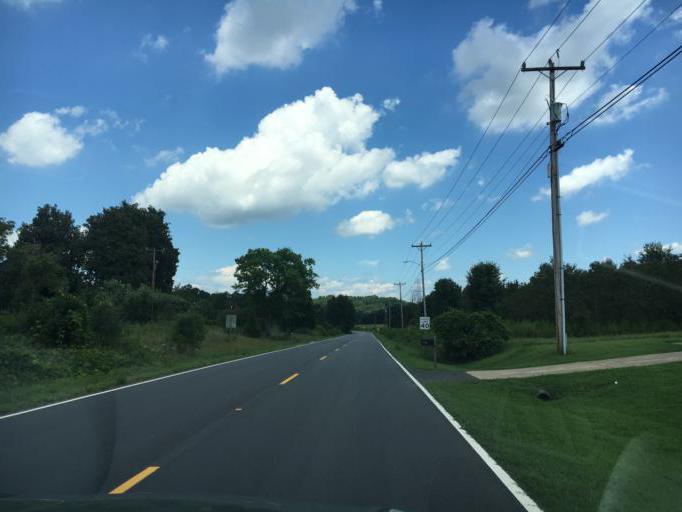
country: US
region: South Carolina
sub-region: Spartanburg County
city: Duncan
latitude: 34.9210
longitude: -82.1441
